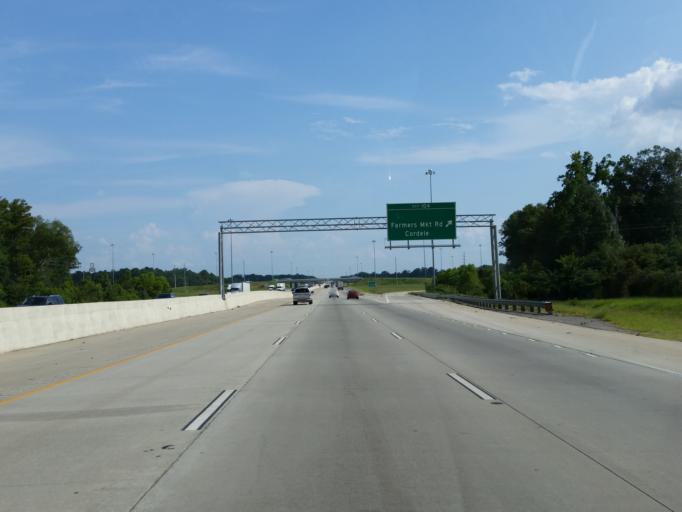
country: US
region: Georgia
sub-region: Crisp County
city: Cordele
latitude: 32.0104
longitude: -83.7596
